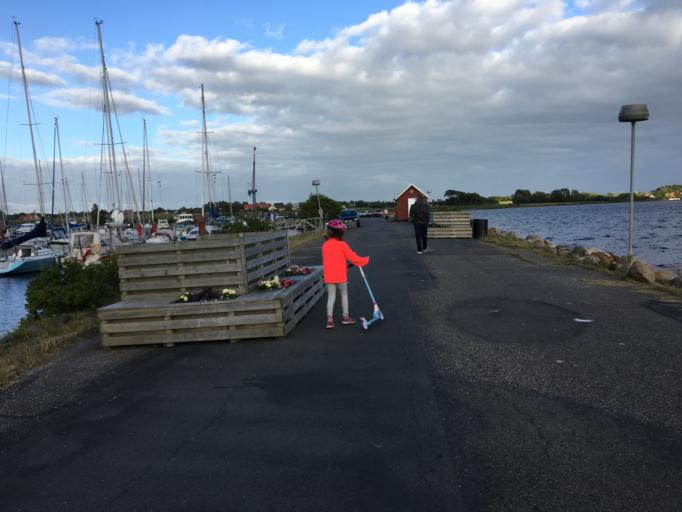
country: DK
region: South Denmark
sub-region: Middelfart Kommune
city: Middelfart
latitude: 55.4907
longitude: 9.7264
